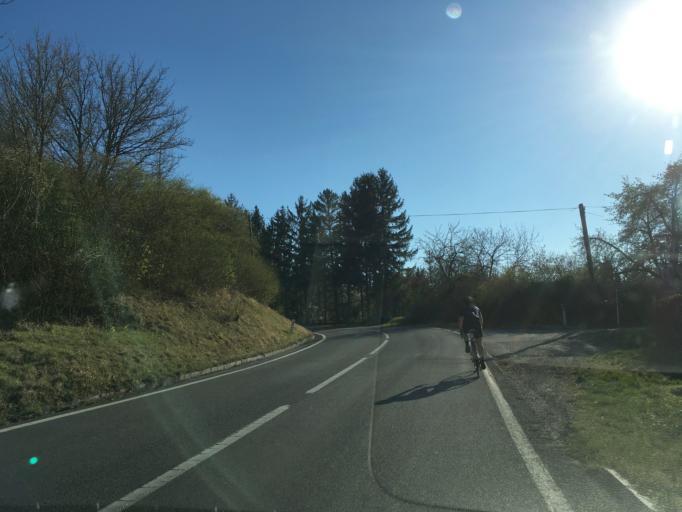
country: AT
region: Lower Austria
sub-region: Politischer Bezirk Tulln
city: Konigstetten
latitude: 48.2994
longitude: 16.1596
